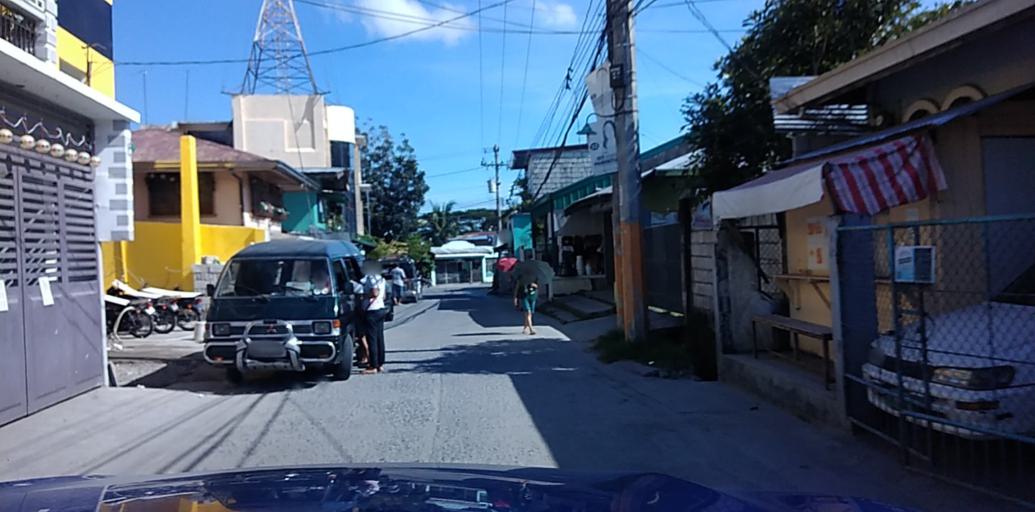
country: PH
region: Central Luzon
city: Santol
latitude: 15.1706
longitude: 120.5147
